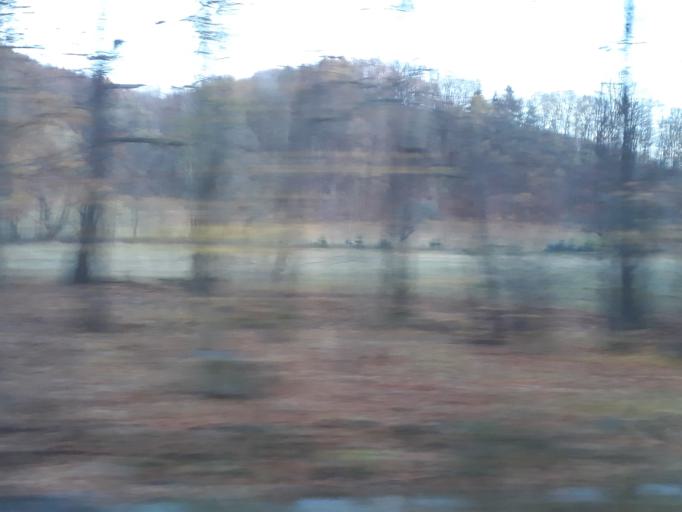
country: DE
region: Saxony
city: Kreischa
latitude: 50.9275
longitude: 13.7763
